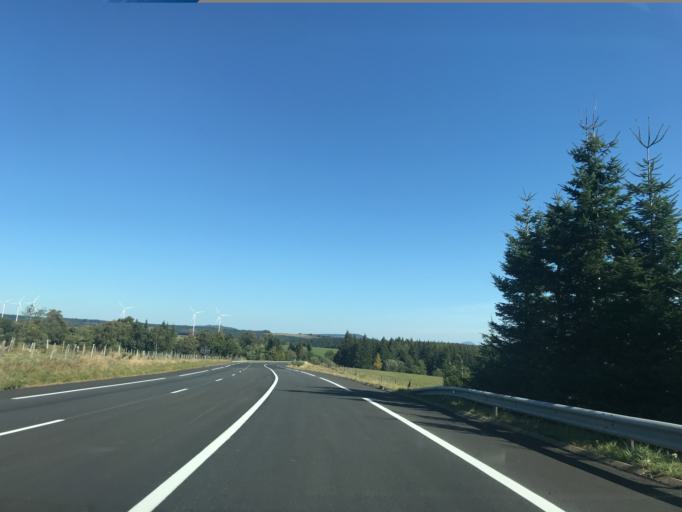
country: FR
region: Auvergne
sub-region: Departement du Puy-de-Dome
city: Saint-Sauves-d'Auvergne
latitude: 45.6573
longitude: 2.7030
